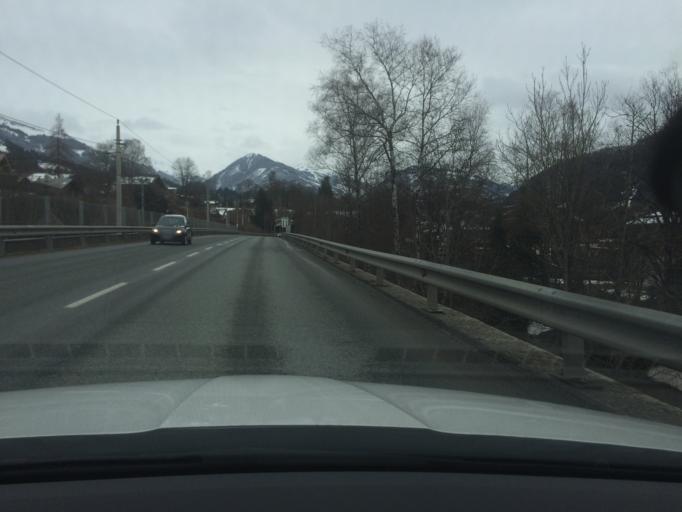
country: AT
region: Tyrol
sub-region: Politischer Bezirk Kitzbuhel
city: Kitzbuhel
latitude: 47.4473
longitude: 12.3961
